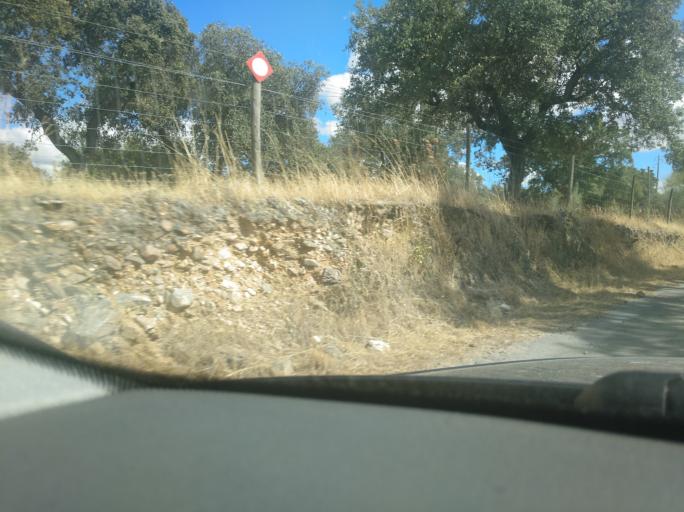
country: ES
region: Extremadura
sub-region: Provincia de Badajoz
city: La Codosera
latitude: 39.1231
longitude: -7.1568
